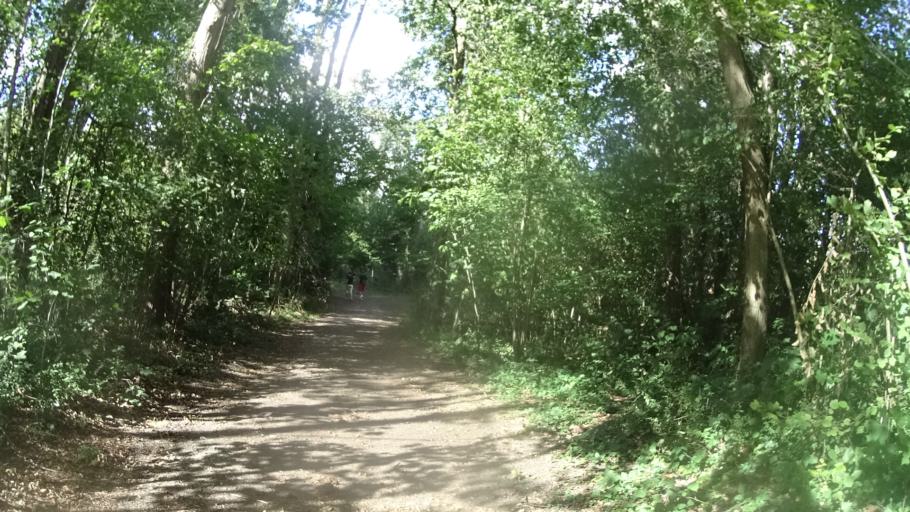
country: FR
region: Ile-de-France
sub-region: Departement de l'Essonne
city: Vert-le-Petit
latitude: 48.5551
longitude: 2.3769
